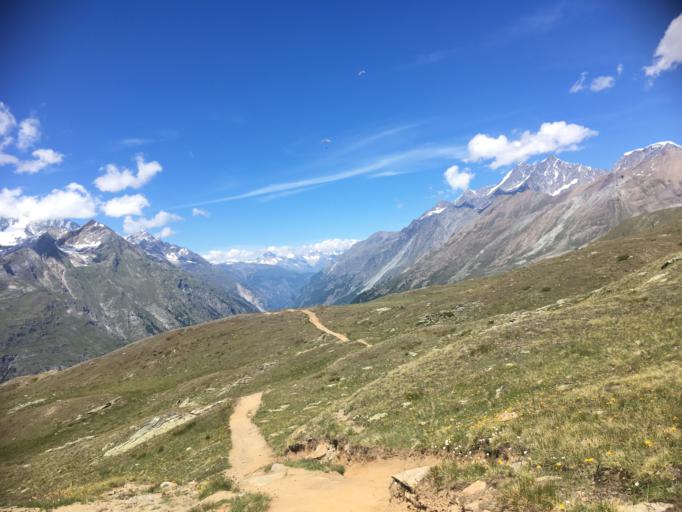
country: CH
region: Valais
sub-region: Visp District
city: Zermatt
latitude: 45.9871
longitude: 7.7516
